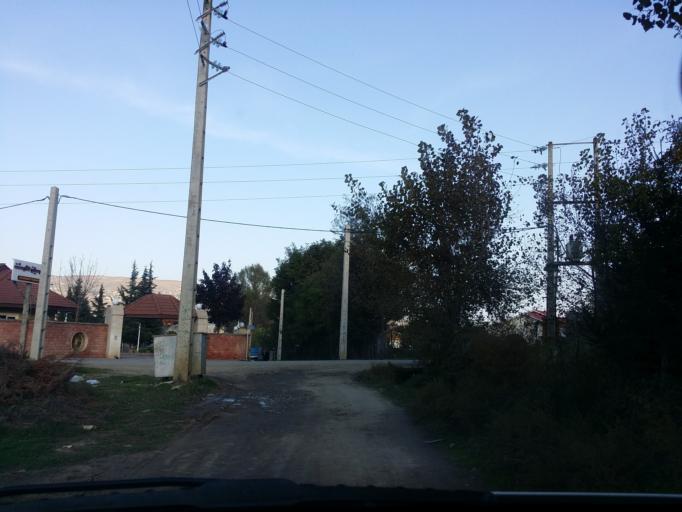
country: IR
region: Mazandaran
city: `Abbasabad
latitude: 36.5105
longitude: 51.1756
